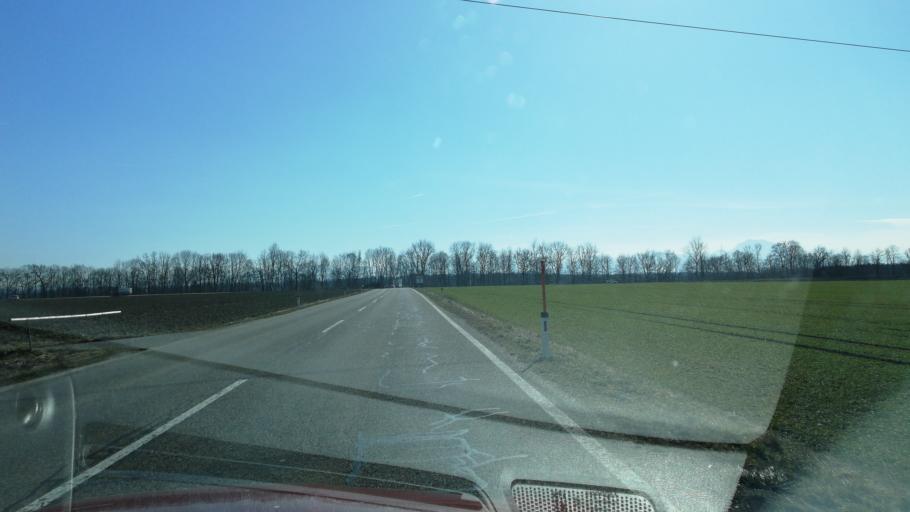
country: AT
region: Upper Austria
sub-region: Wels-Land
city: Neukirchen bei Lambach
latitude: 48.0907
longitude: 13.8400
